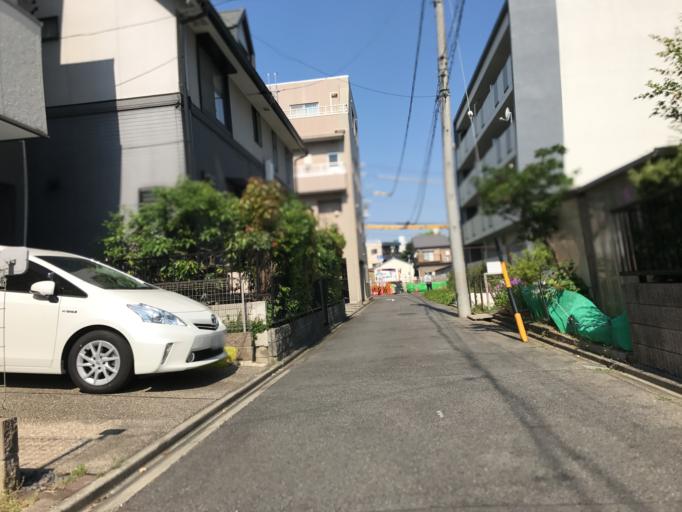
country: JP
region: Aichi
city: Nagoya-shi
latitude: 35.1767
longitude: 136.9257
